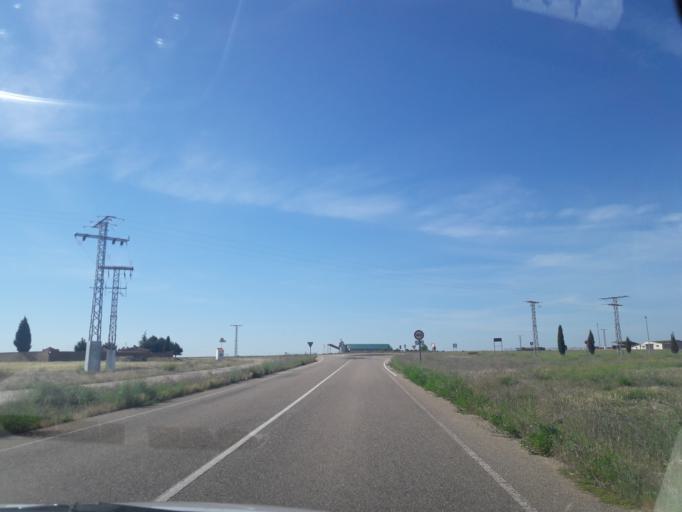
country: ES
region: Castille and Leon
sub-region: Provincia de Salamanca
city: Espino de la Orbada
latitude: 41.0808
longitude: -5.3946
